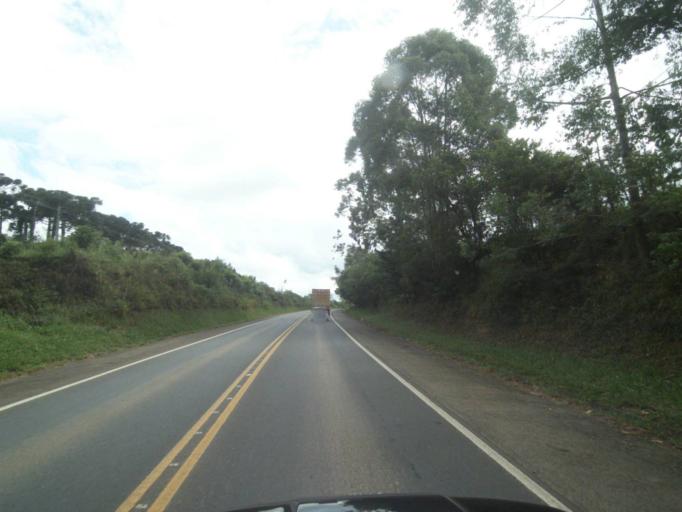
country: BR
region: Parana
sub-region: Telemaco Borba
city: Telemaco Borba
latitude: -24.3665
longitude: -50.6588
